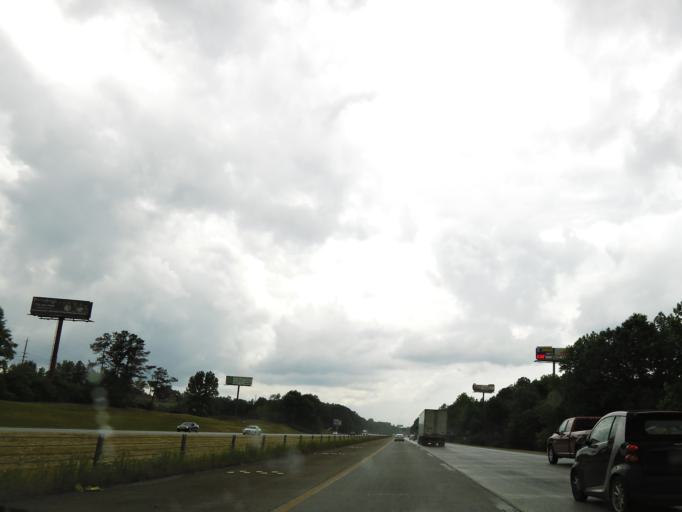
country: US
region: Georgia
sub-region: Carroll County
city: Villa Rica
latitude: 33.7251
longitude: -84.9101
